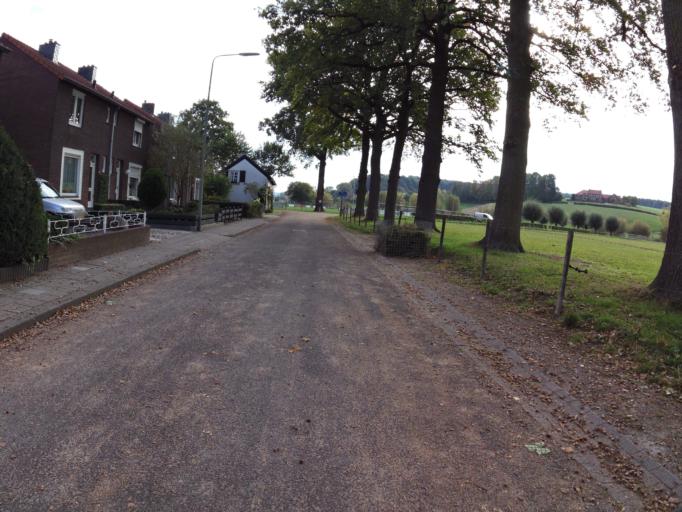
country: NL
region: Limburg
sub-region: Gemeente Voerendaal
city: Ubachsberg
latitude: 50.8086
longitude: 5.9149
